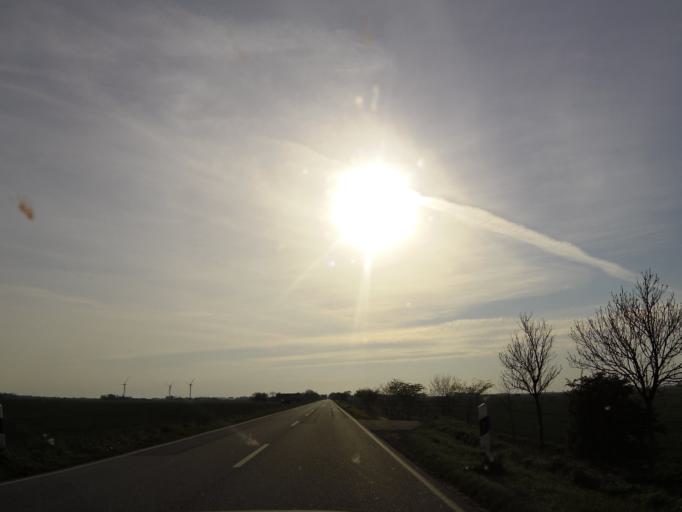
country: DE
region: Schleswig-Holstein
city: Niebull
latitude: 54.7767
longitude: 8.7998
